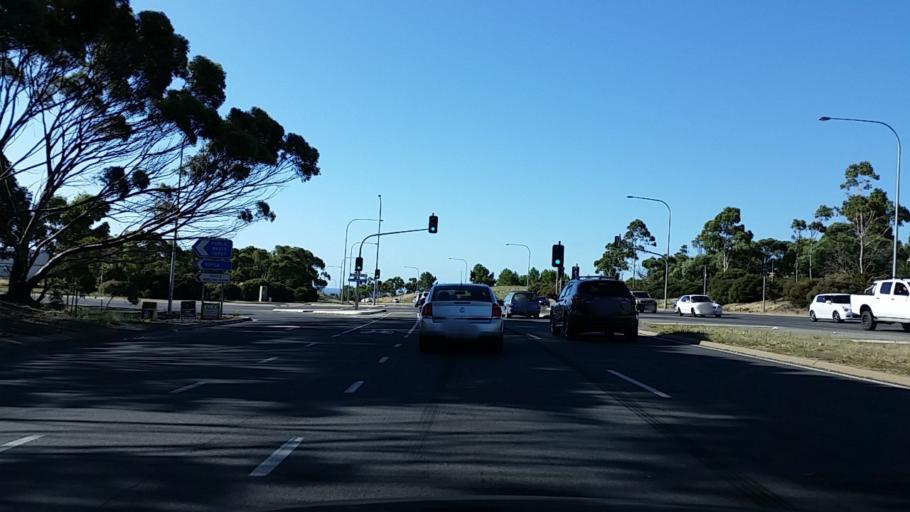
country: AU
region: South Australia
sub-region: Onkaparinga
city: Reynella
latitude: -35.1027
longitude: 138.4998
